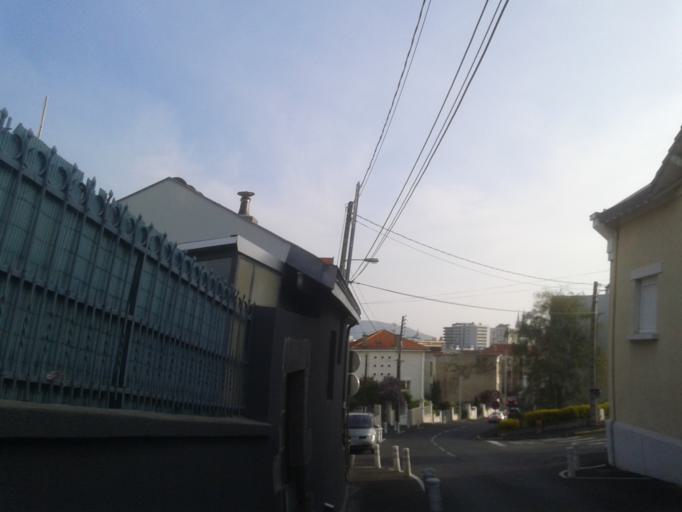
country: FR
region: Auvergne
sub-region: Departement du Puy-de-Dome
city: Chamalieres
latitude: 45.7670
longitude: 3.0727
